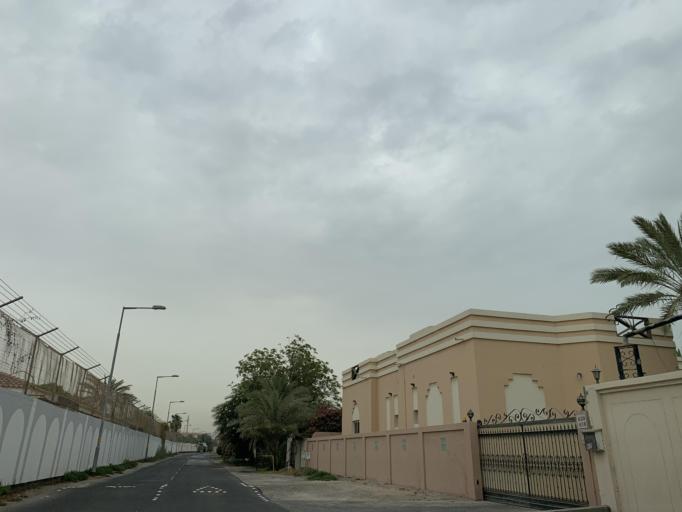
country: BH
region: Northern
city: Madinat `Isa
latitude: 26.1948
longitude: 50.4709
